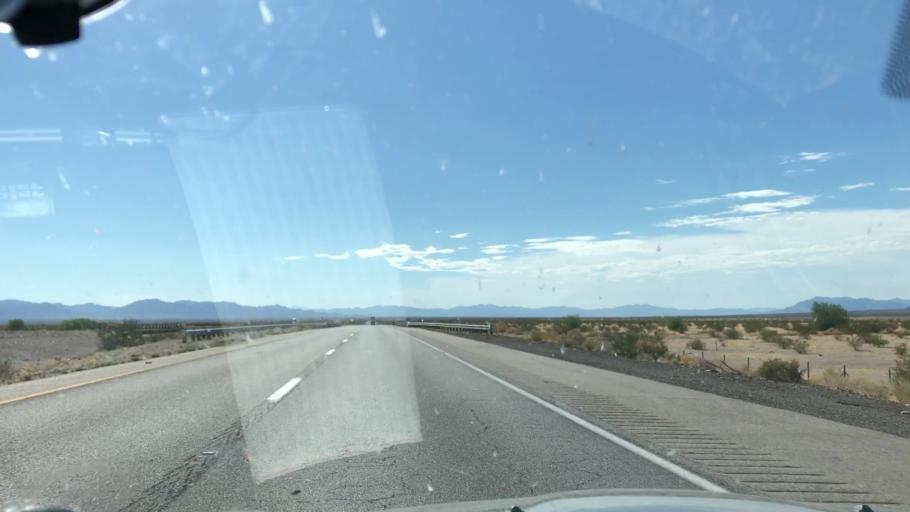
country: US
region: California
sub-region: Riverside County
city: Mesa Verde
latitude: 33.6243
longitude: -115.0484
